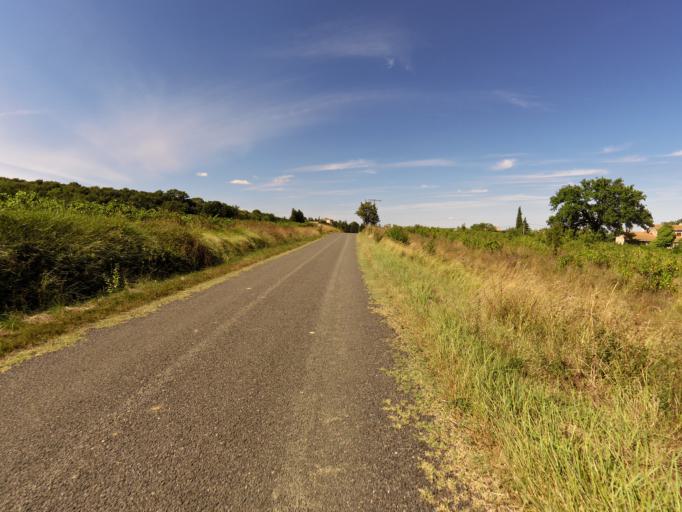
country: FR
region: Languedoc-Roussillon
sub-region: Departement du Gard
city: Quissac
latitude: 43.9512
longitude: 4.0497
